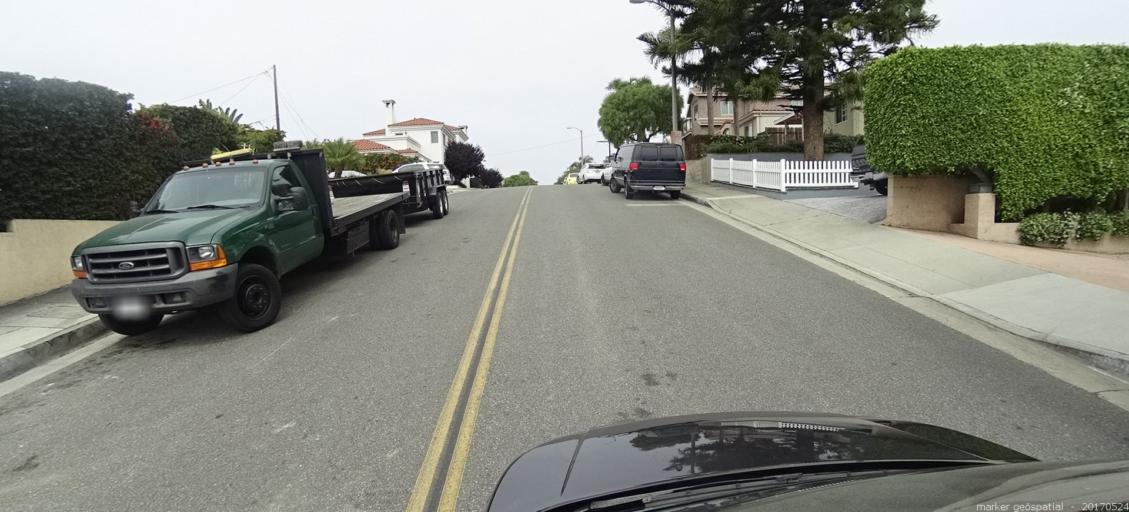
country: US
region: California
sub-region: Los Angeles County
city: Redondo Beach
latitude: 33.8251
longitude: -118.3780
